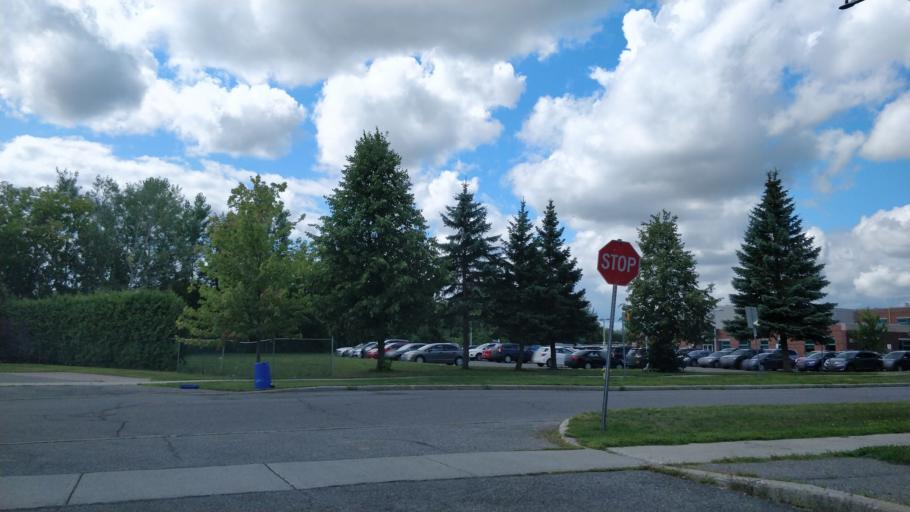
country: CA
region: Ontario
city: Ottawa
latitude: 45.3490
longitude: -75.6330
